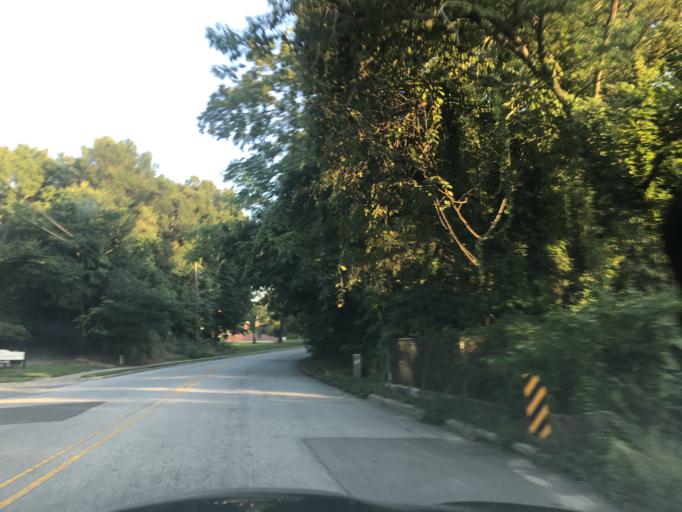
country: US
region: North Carolina
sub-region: Wake County
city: Raleigh
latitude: 35.7980
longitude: -78.6244
